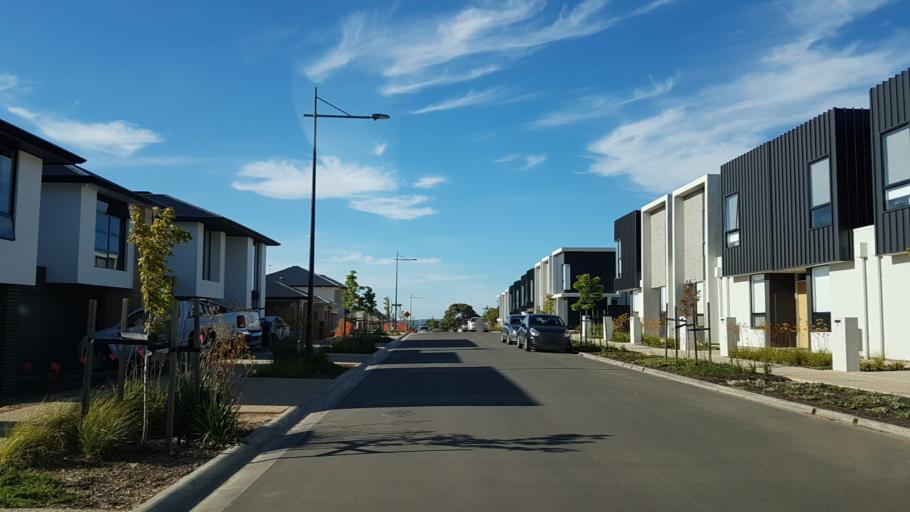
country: AU
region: South Australia
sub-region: Burnside
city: Wattle Park
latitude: -34.9069
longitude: 138.6855
